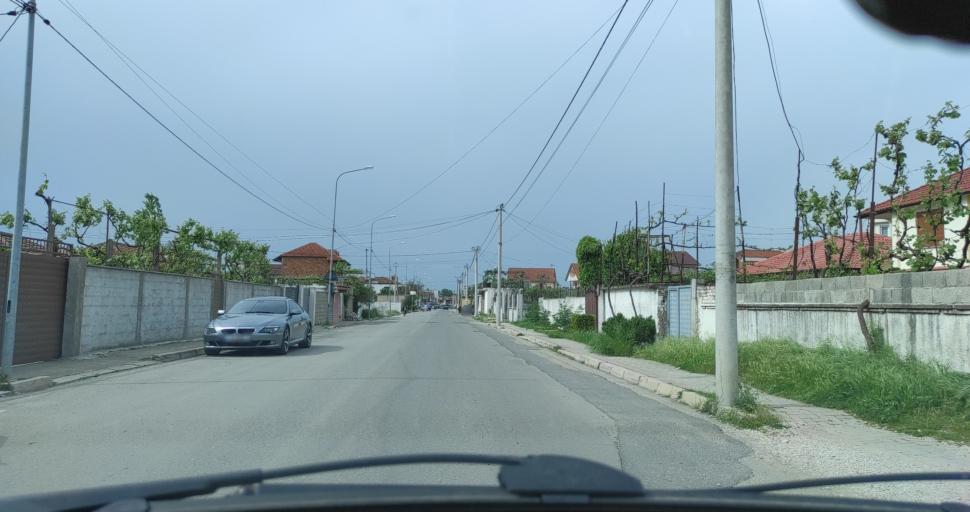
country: AL
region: Durres
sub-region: Rrethi i Krujes
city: Fushe-Kruje
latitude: 41.4740
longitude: 19.7187
